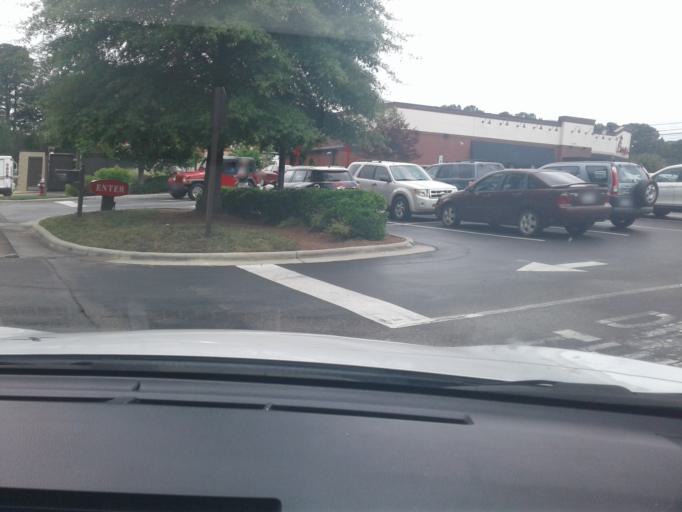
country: US
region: North Carolina
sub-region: Wake County
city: Fuquay-Varina
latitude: 35.5936
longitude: -78.7673
